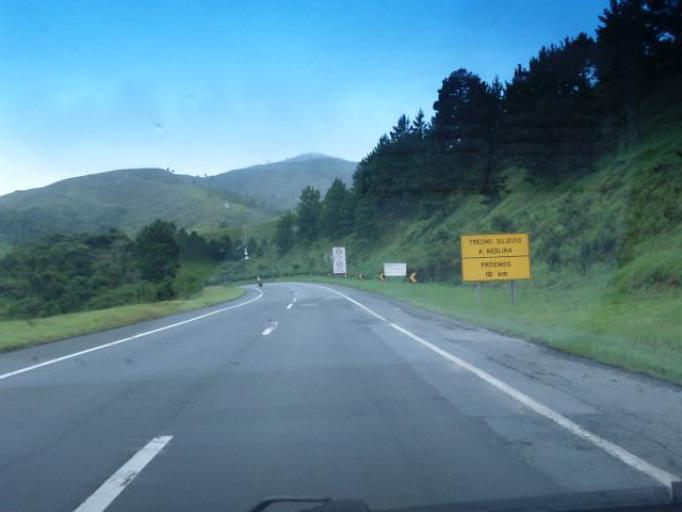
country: BR
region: Sao Paulo
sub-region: Cajati
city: Cajati
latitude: -24.9765
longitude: -48.4989
